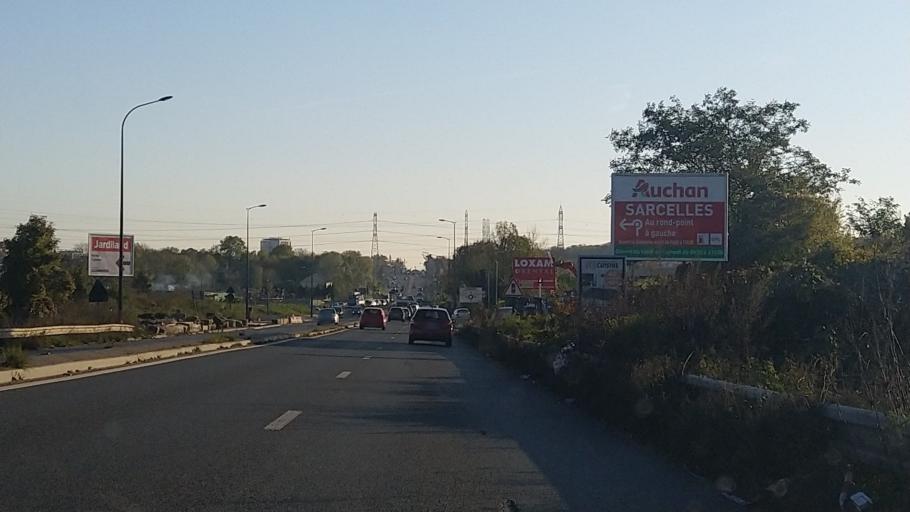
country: FR
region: Ile-de-France
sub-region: Departement du Val-d'Oise
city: Groslay
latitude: 48.9882
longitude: 2.3602
